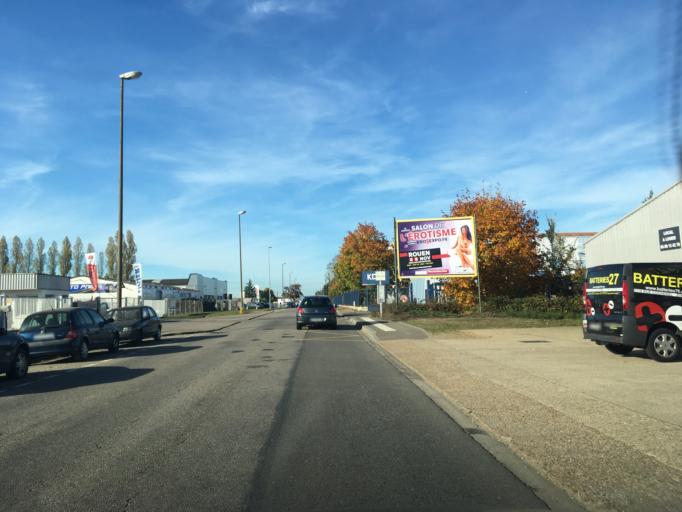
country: FR
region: Haute-Normandie
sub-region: Departement de l'Eure
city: Evreux
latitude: 49.0172
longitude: 1.1858
